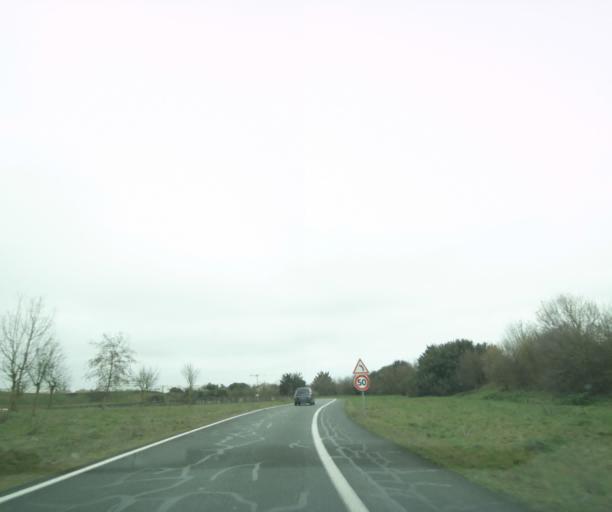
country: FR
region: Poitou-Charentes
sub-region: Departement de la Charente-Maritime
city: Puilboreau
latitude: 46.1770
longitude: -1.1276
